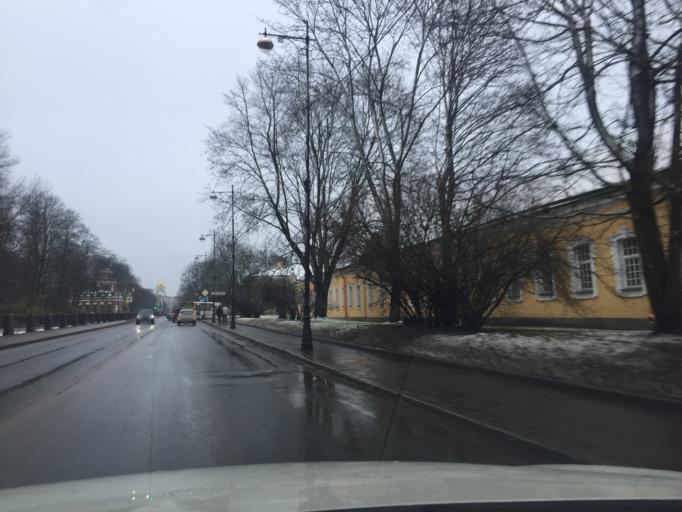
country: RU
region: St.-Petersburg
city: Pushkin
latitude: 59.7138
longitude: 30.4081
